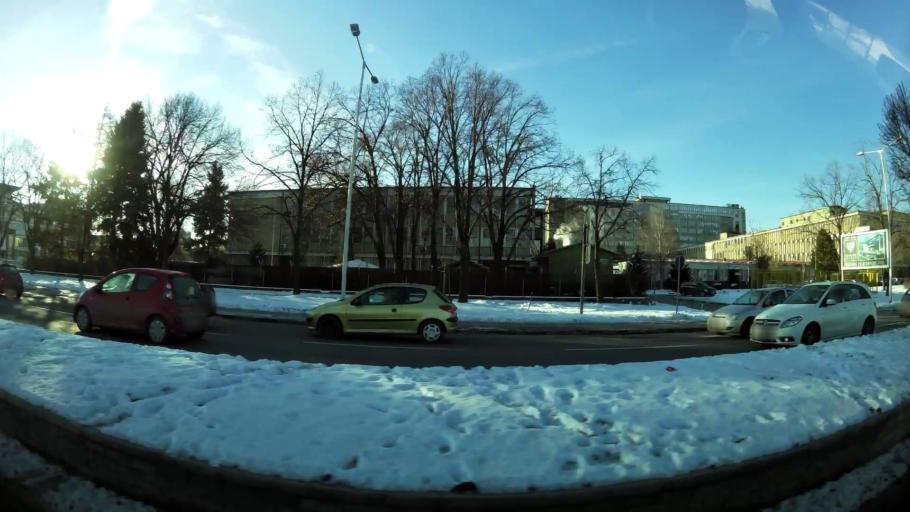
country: MK
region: Karpos
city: Skopje
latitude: 42.0071
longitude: 21.4048
